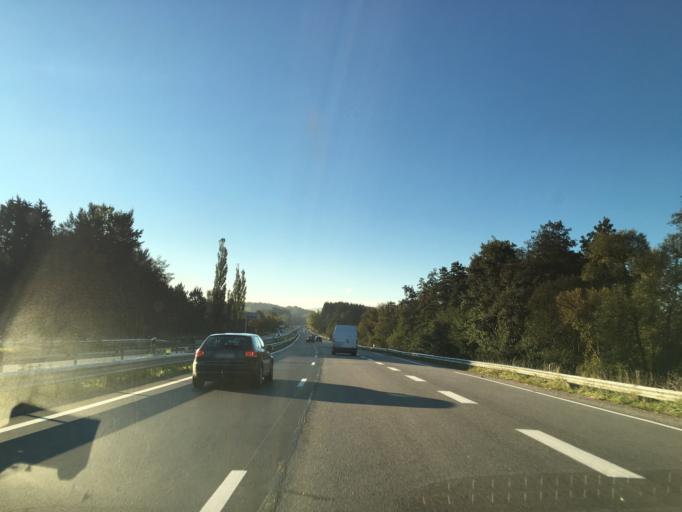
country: FR
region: Lorraine
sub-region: Departement des Vosges
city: Etival-Clairefontaine
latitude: 48.3523
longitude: 6.8836
